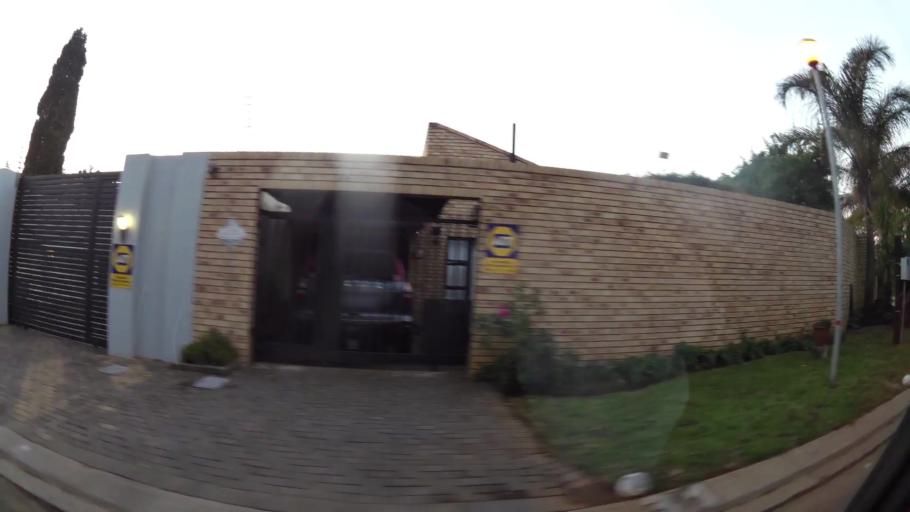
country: ZA
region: Gauteng
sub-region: City of Johannesburg Metropolitan Municipality
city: Diepsloot
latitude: -26.0304
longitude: 28.0206
